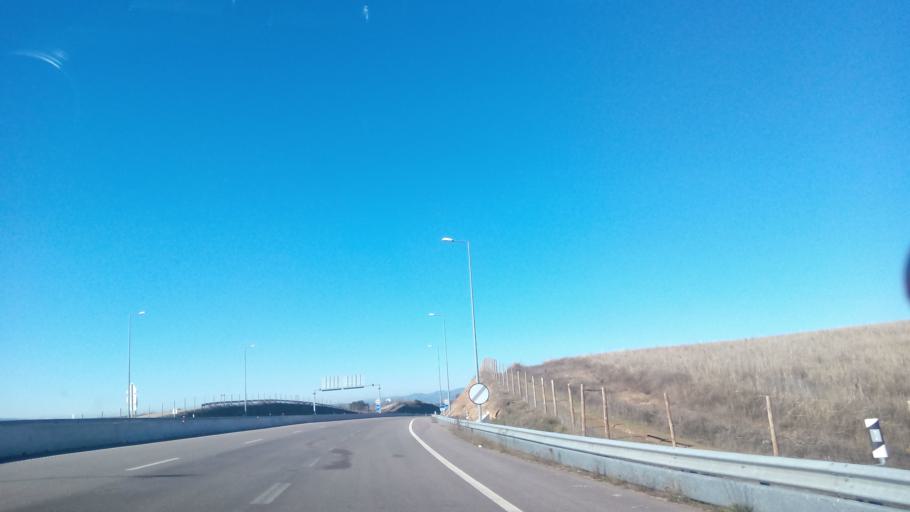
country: ES
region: Castille and Leon
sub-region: Provincia de Zamora
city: Trabazos
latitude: 41.7463
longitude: -6.6249
